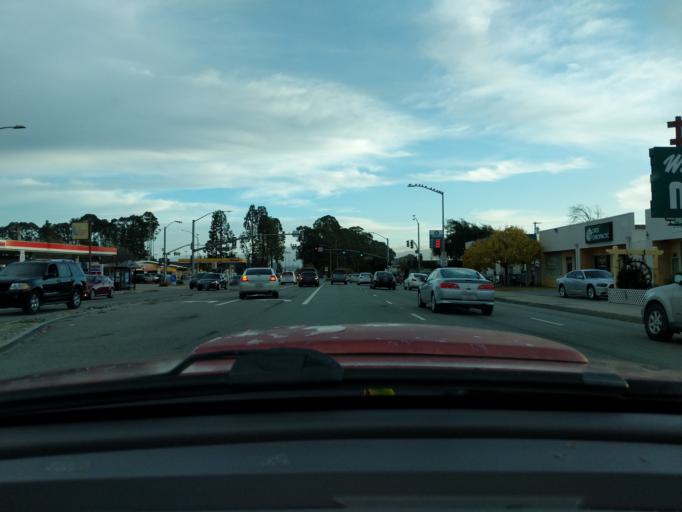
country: US
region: California
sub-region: Monterey County
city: Salinas
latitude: 36.7002
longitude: -121.6522
